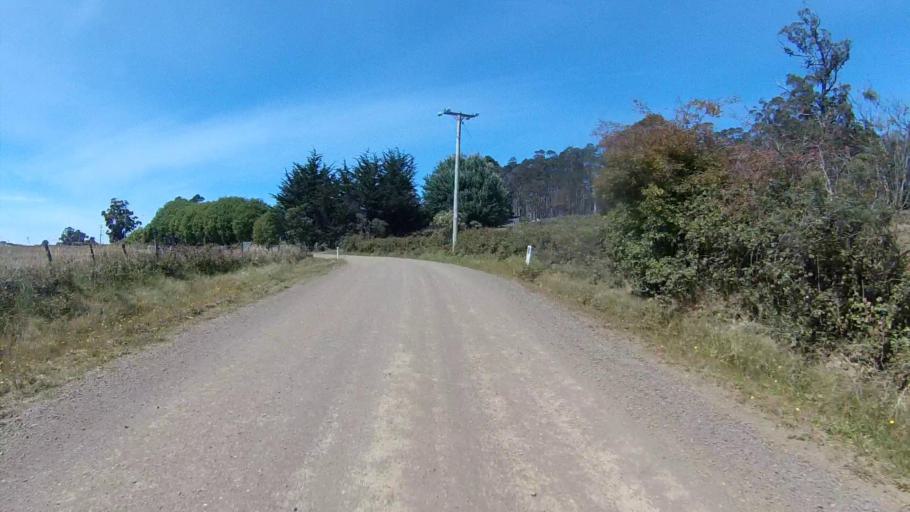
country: AU
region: Tasmania
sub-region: Sorell
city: Sorell
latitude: -42.7042
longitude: 147.7430
